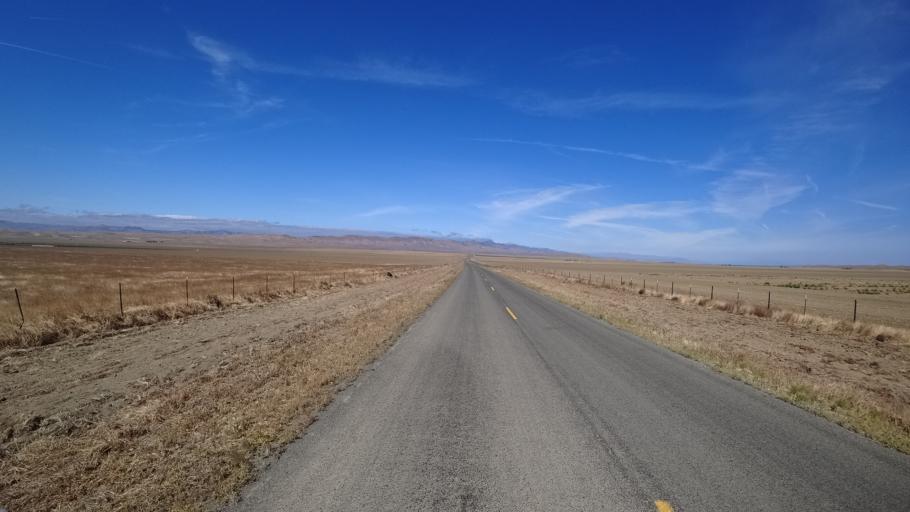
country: US
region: California
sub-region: Kings County
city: Kettleman City
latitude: 35.9353
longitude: -120.0288
